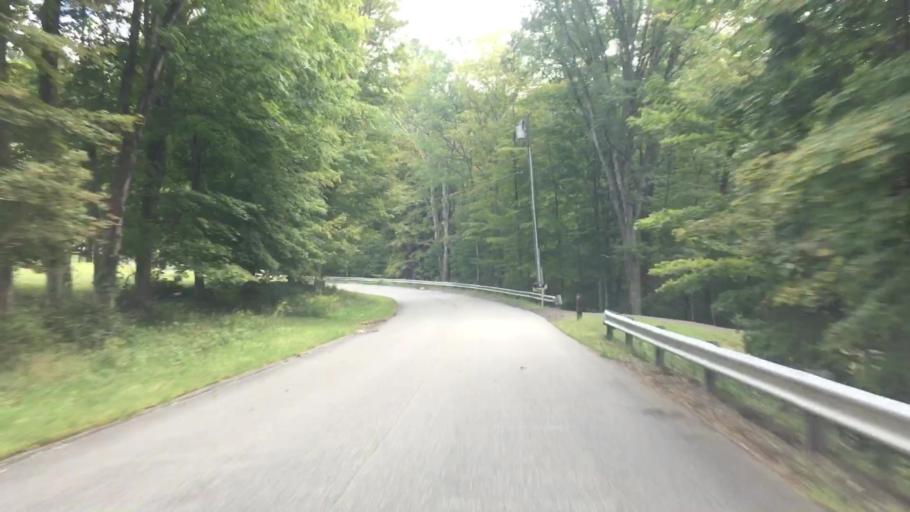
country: US
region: Connecticut
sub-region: Tolland County
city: Stafford Springs
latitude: 41.9174
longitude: -72.2238
